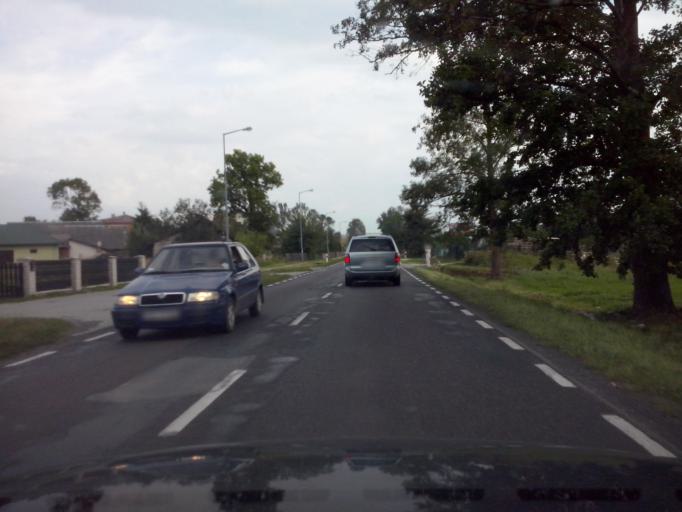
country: PL
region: Lublin Voivodeship
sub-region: Powiat bilgorajski
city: Bilgoraj
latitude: 50.5039
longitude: 22.7221
